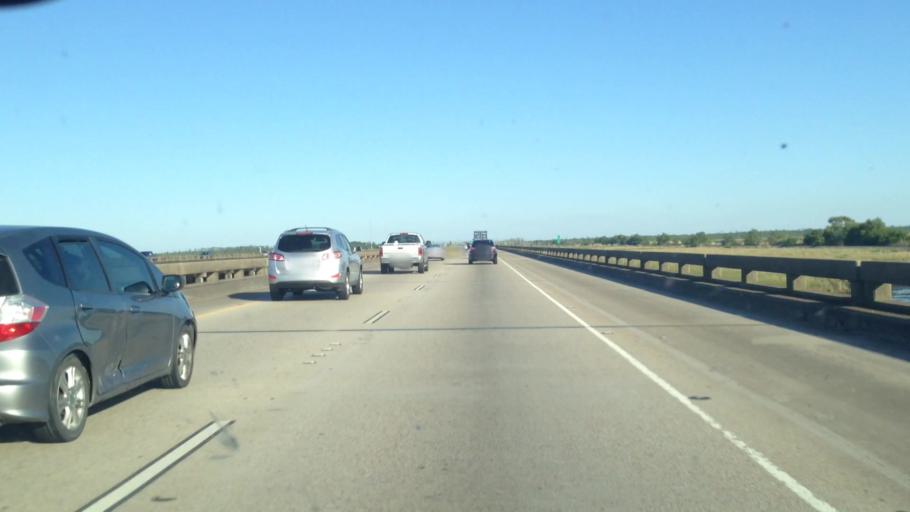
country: US
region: Louisiana
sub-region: Saint Charles Parish
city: Ama
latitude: 30.0204
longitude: -90.3203
